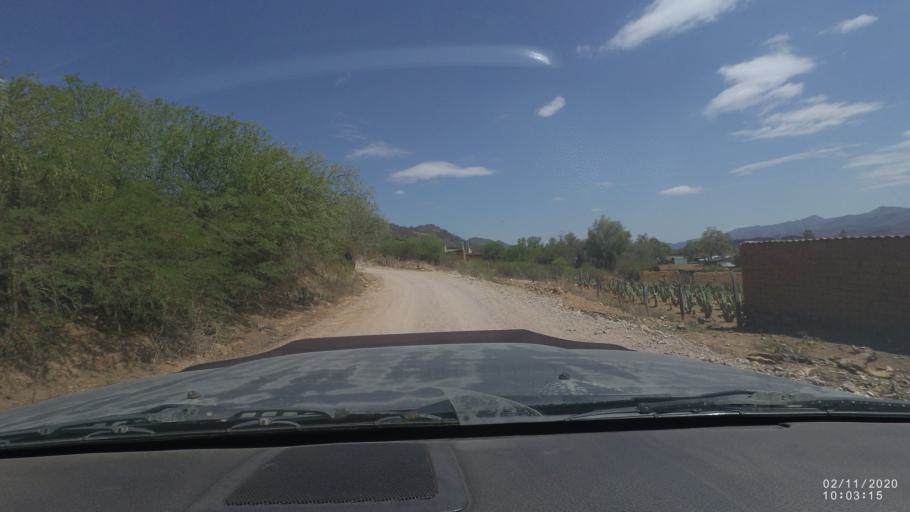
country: BO
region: Chuquisaca
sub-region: Provincia Zudanez
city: Mojocoya
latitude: -18.3249
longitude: -64.6756
